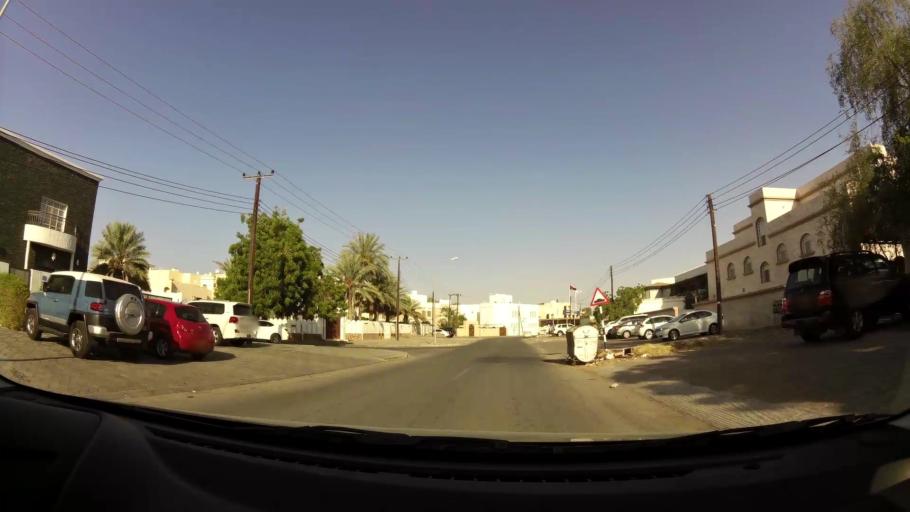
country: OM
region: Muhafazat Masqat
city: As Sib al Jadidah
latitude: 23.6369
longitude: 58.2040
